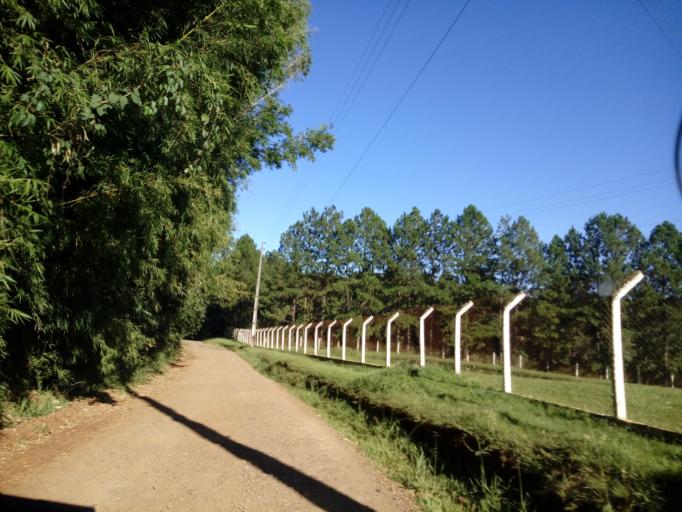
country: BR
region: Santa Catarina
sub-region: Chapeco
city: Chapeco
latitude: -27.2049
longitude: -52.6959
